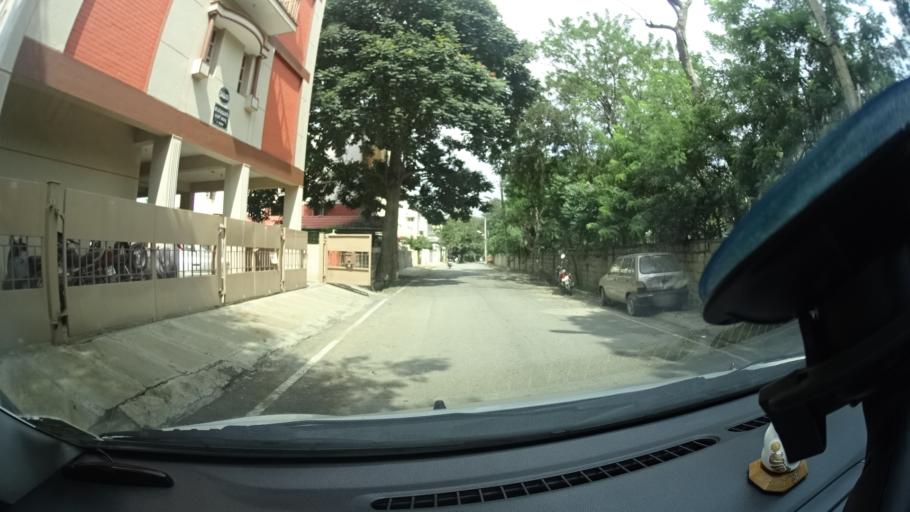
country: IN
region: Karnataka
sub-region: Bangalore Urban
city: Yelahanka
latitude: 13.1041
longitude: 77.5811
